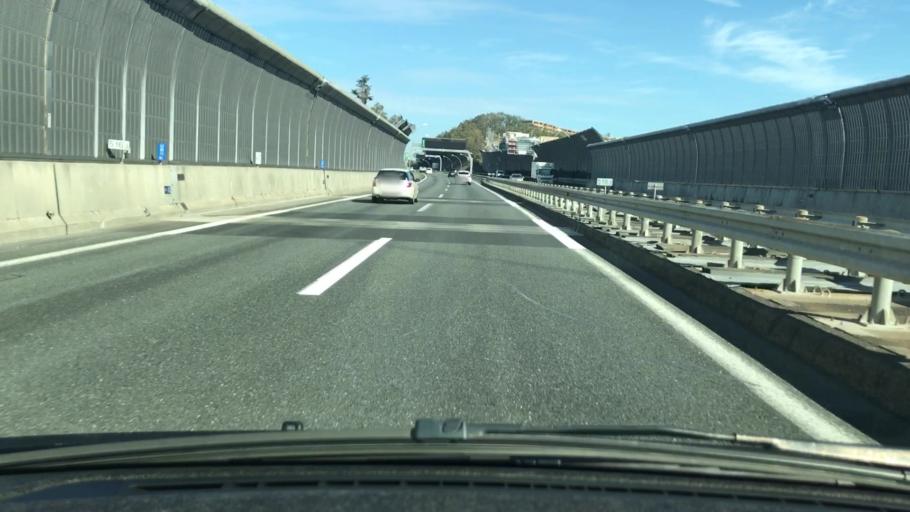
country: JP
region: Osaka
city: Suita
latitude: 34.7933
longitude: 135.5365
